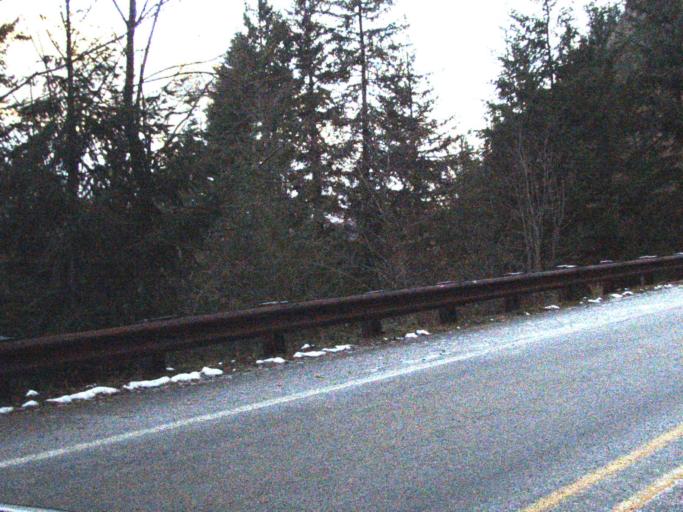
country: US
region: Washington
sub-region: Snohomish County
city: Darrington
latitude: 48.7108
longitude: -121.0812
